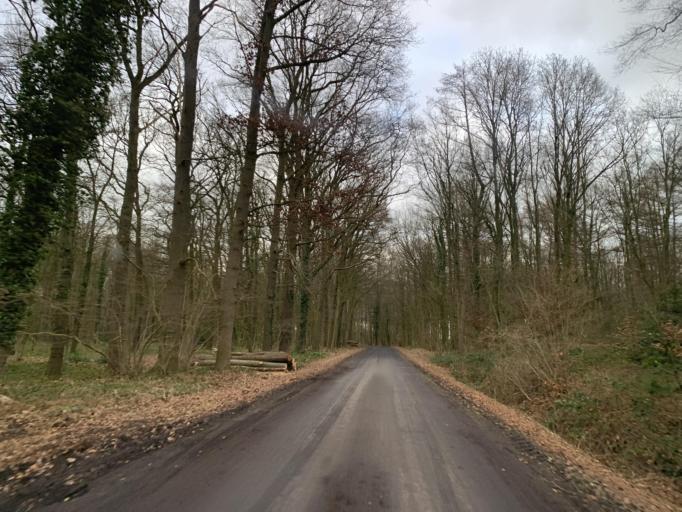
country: DE
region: North Rhine-Westphalia
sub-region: Regierungsbezirk Munster
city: Ascheberg
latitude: 51.8057
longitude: 7.5825
